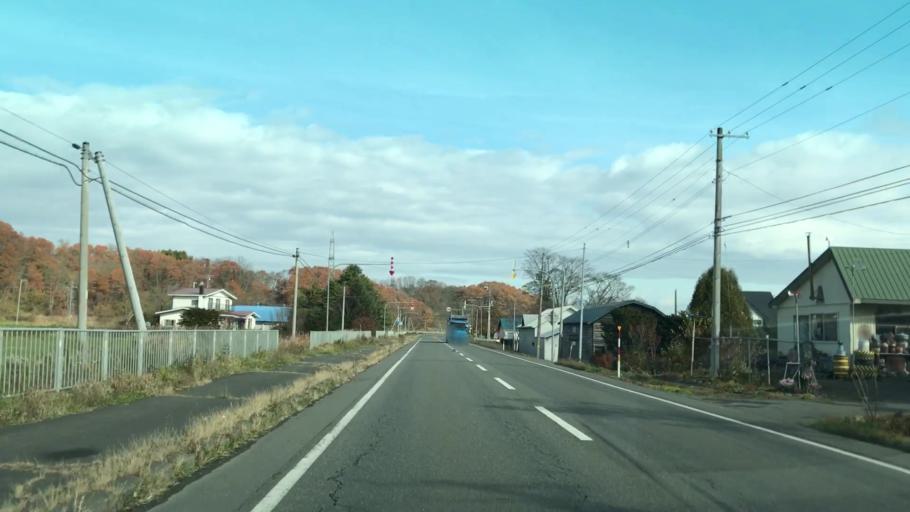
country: JP
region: Hokkaido
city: Shizunai-furukawacho
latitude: 42.5576
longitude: 142.0794
